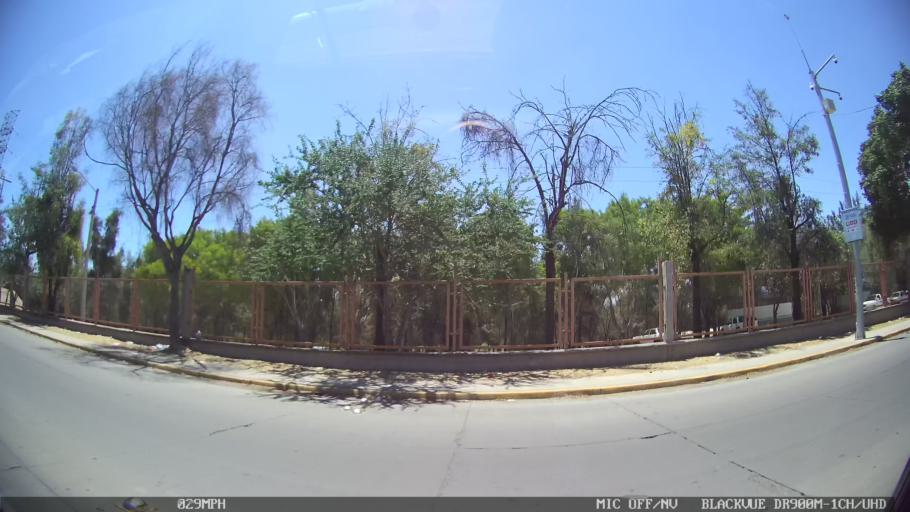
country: MX
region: Jalisco
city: Tlaquepaque
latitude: 20.6743
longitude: -103.2691
